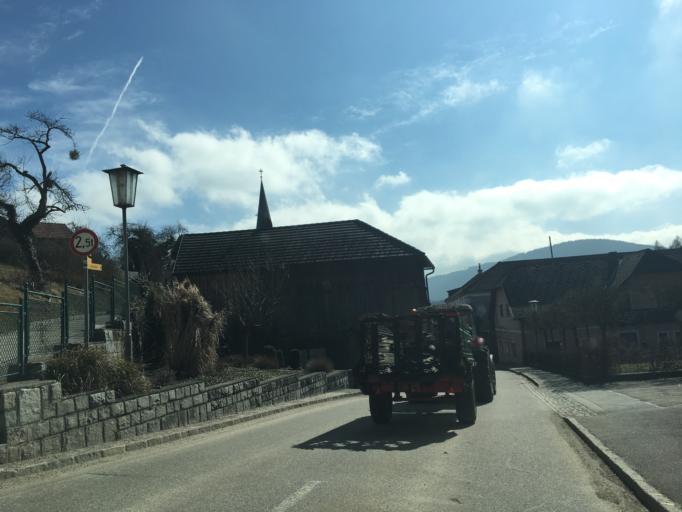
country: AT
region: Lower Austria
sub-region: Politischer Bezirk Melk
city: Nochling
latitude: 48.2741
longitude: 14.9472
